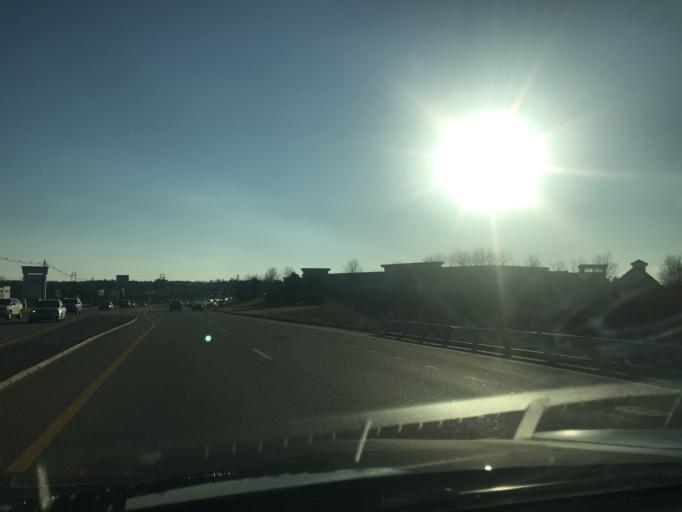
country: US
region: Massachusetts
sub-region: Plymouth County
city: North Plymouth
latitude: 41.9558
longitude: -70.7113
